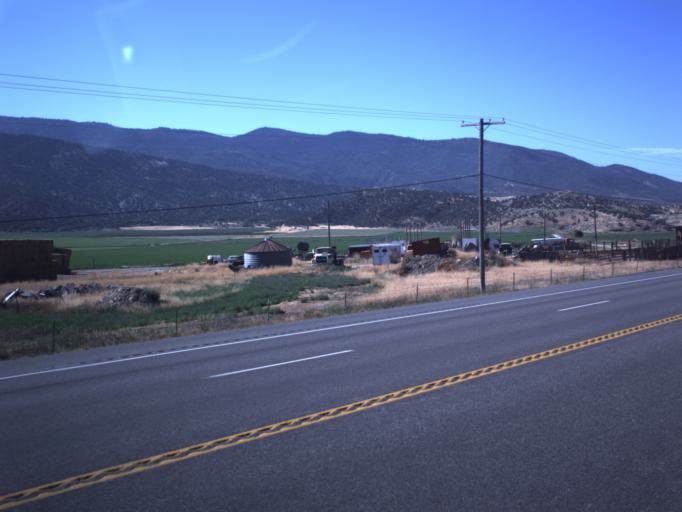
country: US
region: Utah
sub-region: Sanpete County
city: Manti
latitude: 39.2895
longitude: -111.6251
